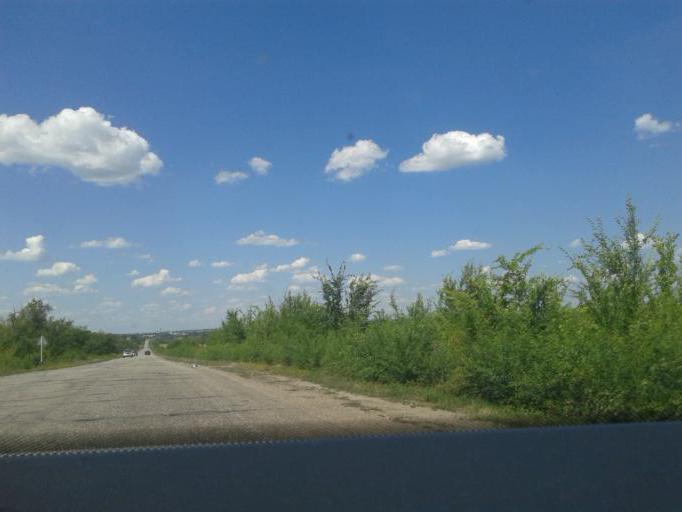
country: RU
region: Volgograd
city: Frolovo
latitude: 49.7251
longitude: 43.6589
